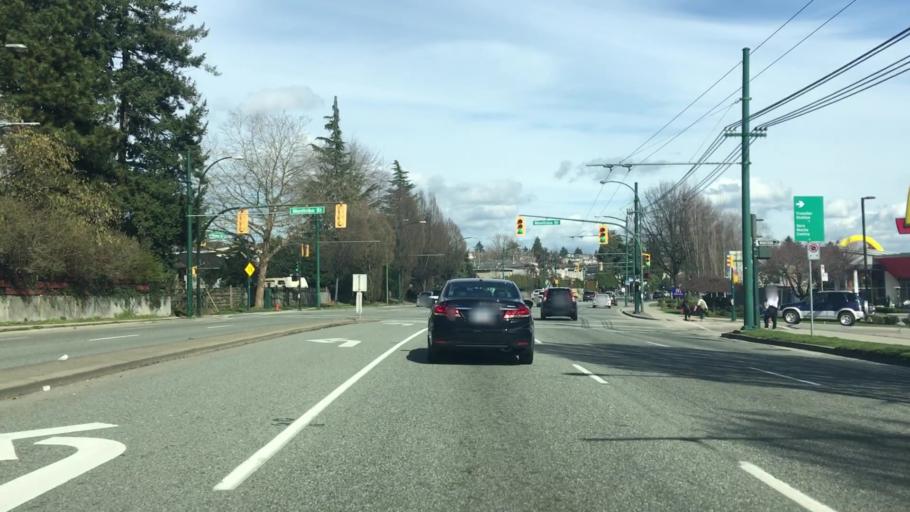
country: CA
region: British Columbia
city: Vancouver
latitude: 49.2120
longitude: -123.1106
